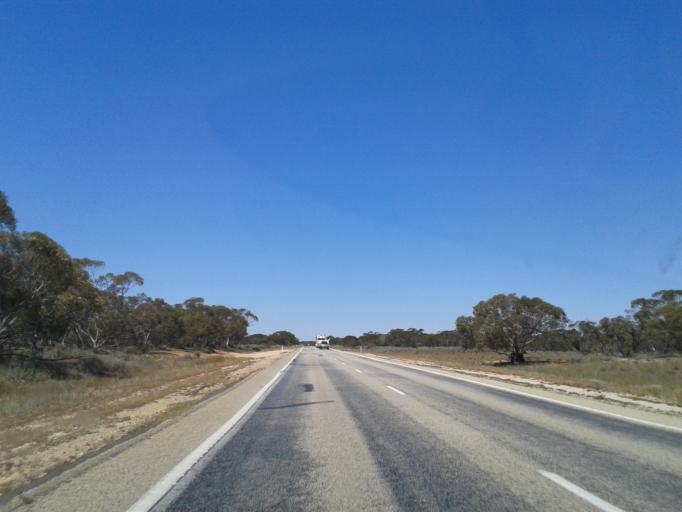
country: AU
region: New South Wales
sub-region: Wentworth
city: Gol Gol
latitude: -34.4205
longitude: 142.4487
